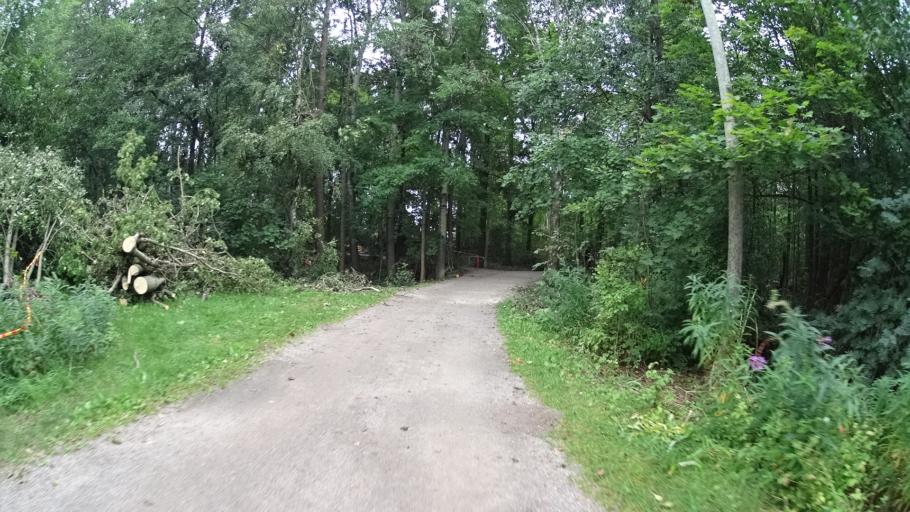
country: FI
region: Uusimaa
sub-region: Helsinki
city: Teekkarikylae
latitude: 60.2098
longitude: 24.8516
